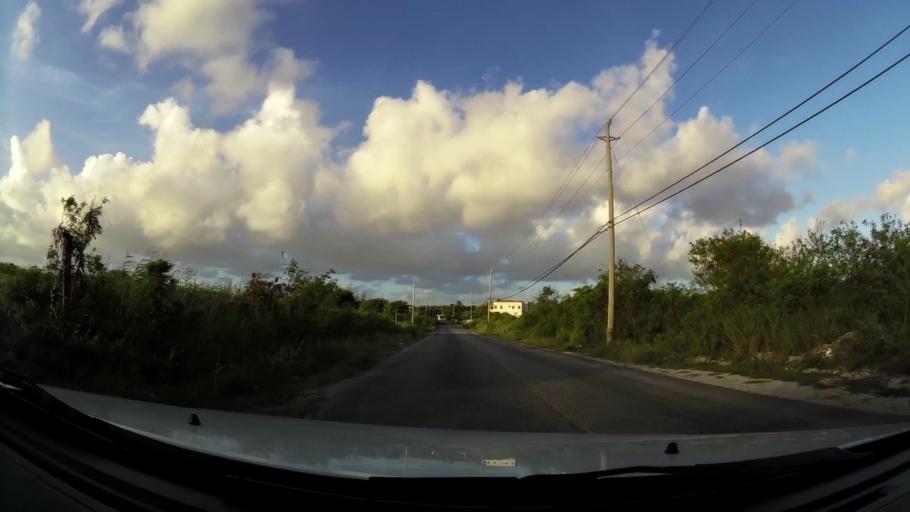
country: BB
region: Saint Philip
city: Crane
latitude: 13.0904
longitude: -59.4719
